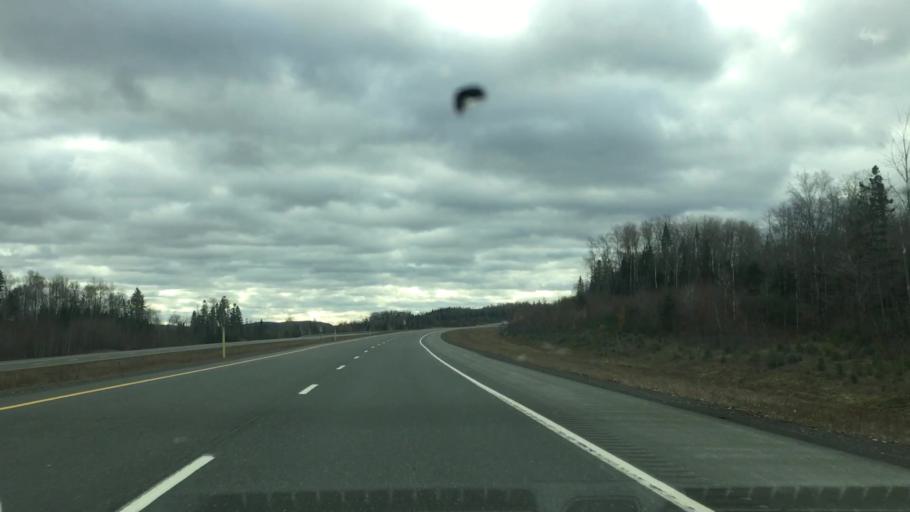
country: US
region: Maine
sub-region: Aroostook County
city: Fort Fairfield
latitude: 46.6739
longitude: -67.7297
